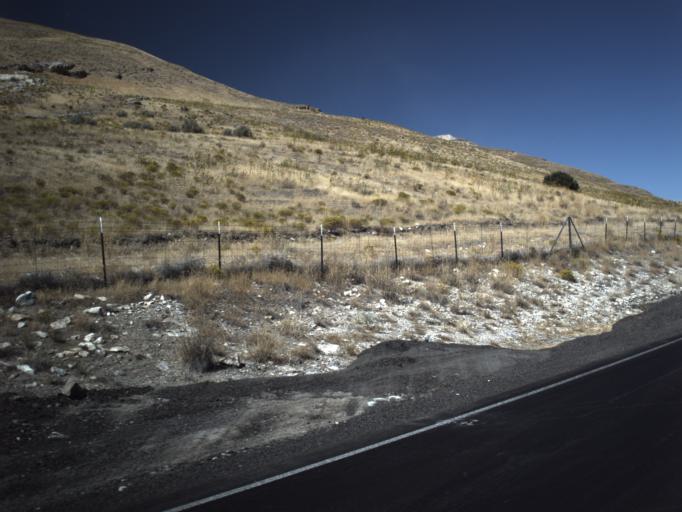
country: US
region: Utah
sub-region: Utah County
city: Saratoga Springs
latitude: 40.2400
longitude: -111.8670
